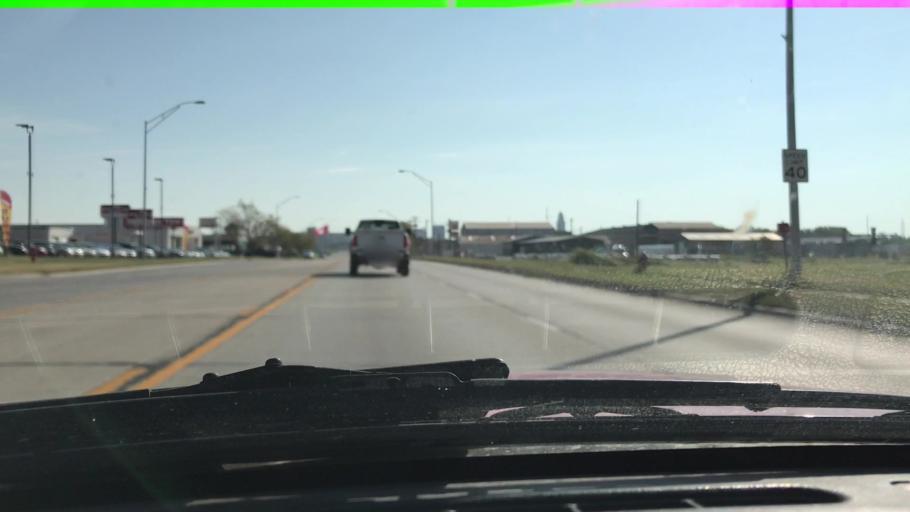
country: US
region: Nebraska
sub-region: Lancaster County
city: Lincoln
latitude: 40.8137
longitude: -96.7314
